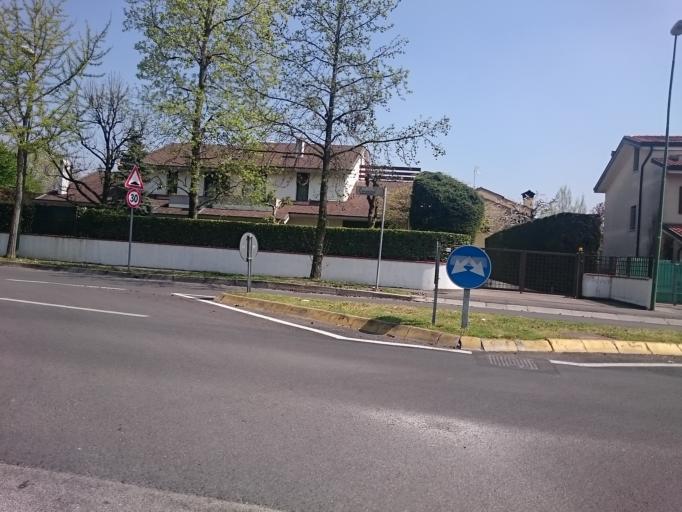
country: IT
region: Veneto
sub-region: Provincia di Padova
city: Caselle
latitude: 45.4159
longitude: 11.8148
